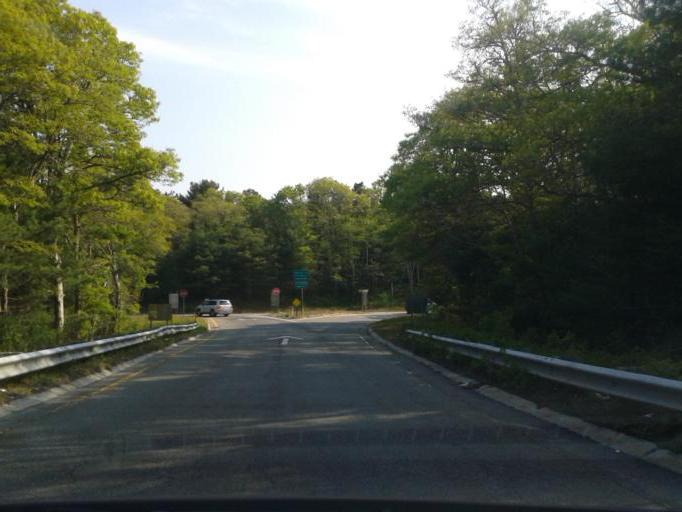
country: US
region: Massachusetts
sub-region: Barnstable County
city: West Falmouth
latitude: 41.5952
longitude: -70.6287
